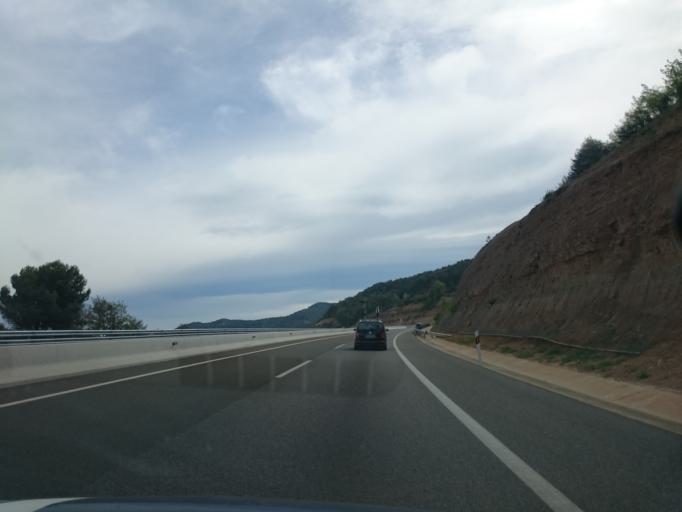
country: ES
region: Catalonia
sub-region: Provincia de Barcelona
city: Orista
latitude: 41.9071
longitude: 2.1128
